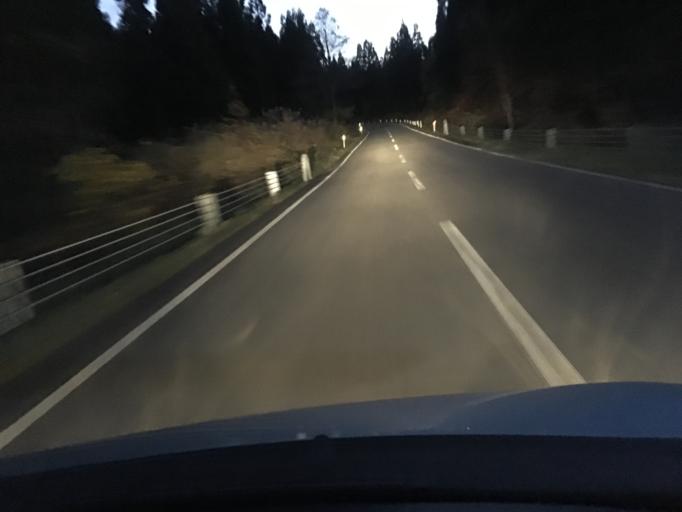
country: JP
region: Akita
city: Yuzawa
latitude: 38.9749
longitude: 140.7102
